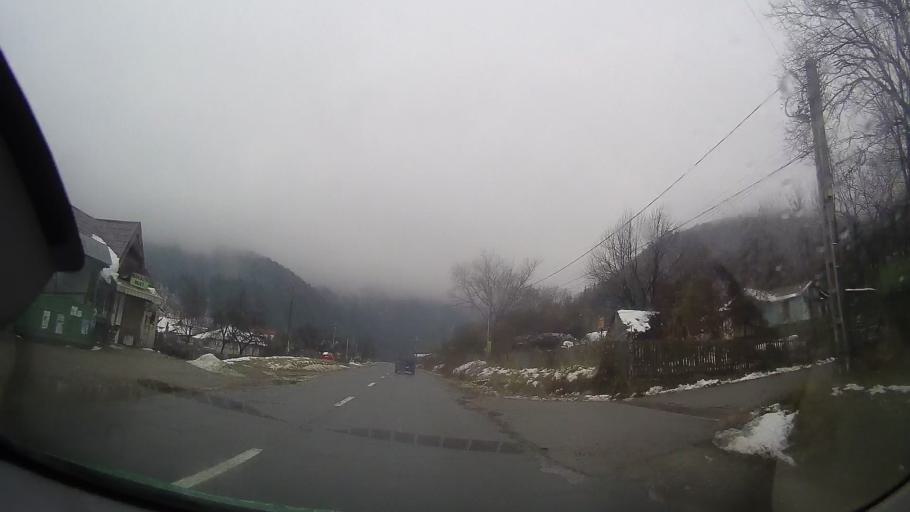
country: RO
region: Neamt
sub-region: Comuna Pangarati
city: Stejaru
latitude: 46.8966
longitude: 26.1705
